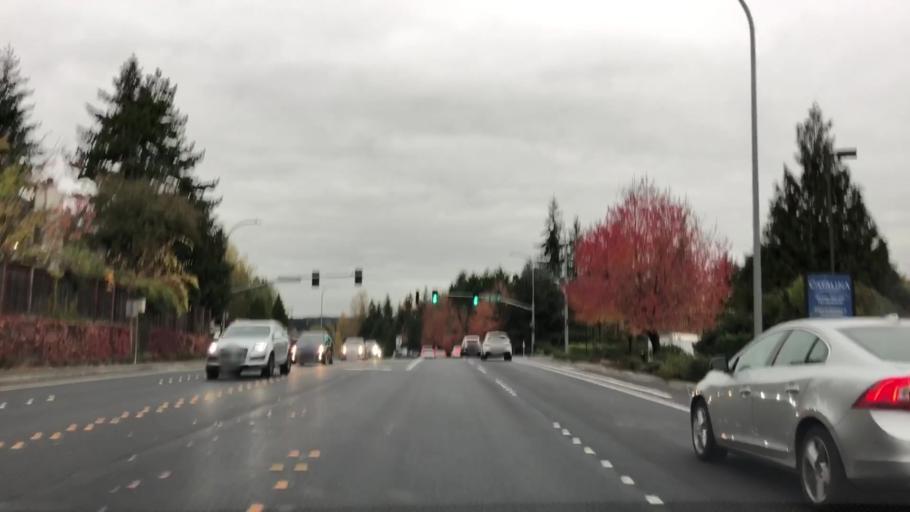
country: US
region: Washington
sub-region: King County
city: Newport
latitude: 47.5910
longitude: -122.1642
